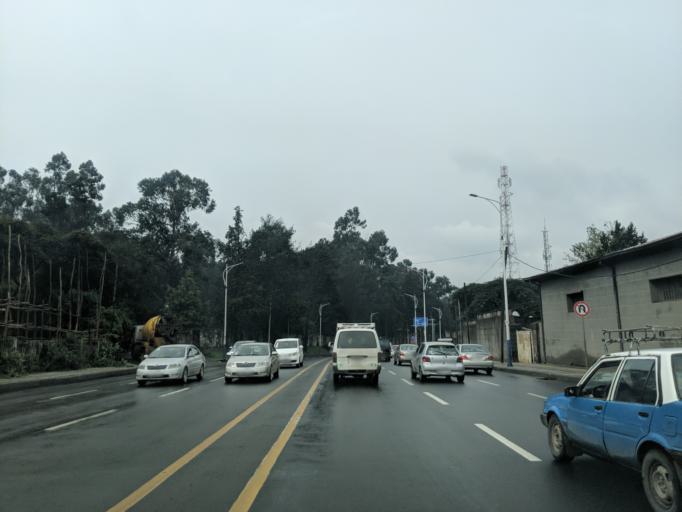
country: ET
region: Adis Abeba
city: Addis Ababa
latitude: 9.0284
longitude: 38.7632
